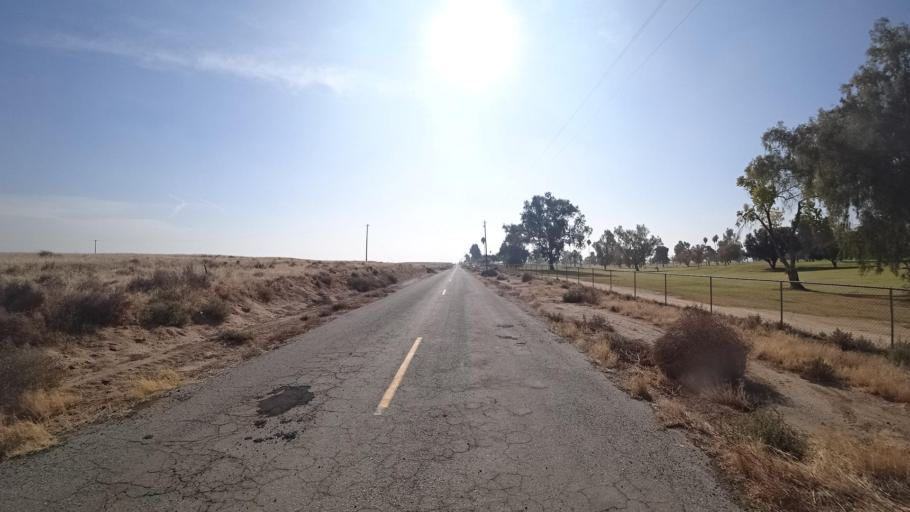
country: US
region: California
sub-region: Kern County
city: Oildale
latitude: 35.5203
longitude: -119.1087
